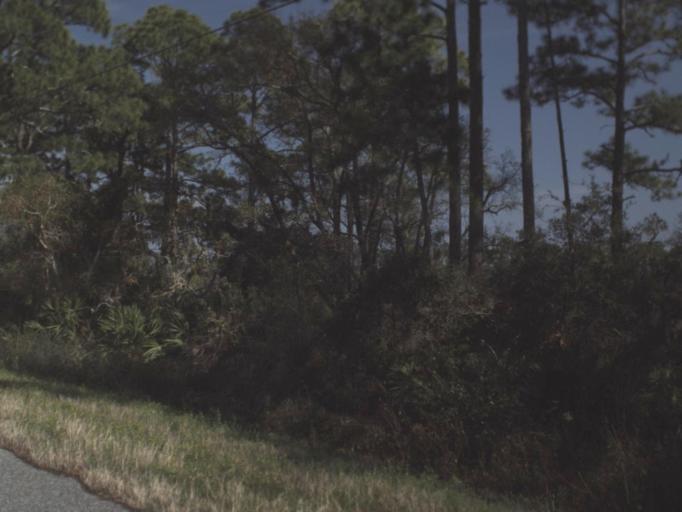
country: US
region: Florida
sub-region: Franklin County
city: Carrabelle
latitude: 29.7912
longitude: -84.7597
